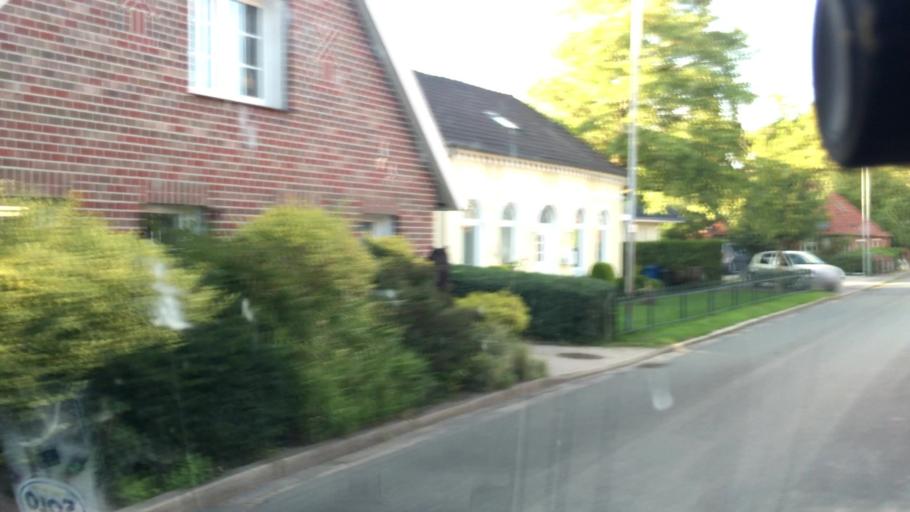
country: DE
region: Lower Saxony
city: Werdum
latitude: 53.6525
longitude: 7.7797
